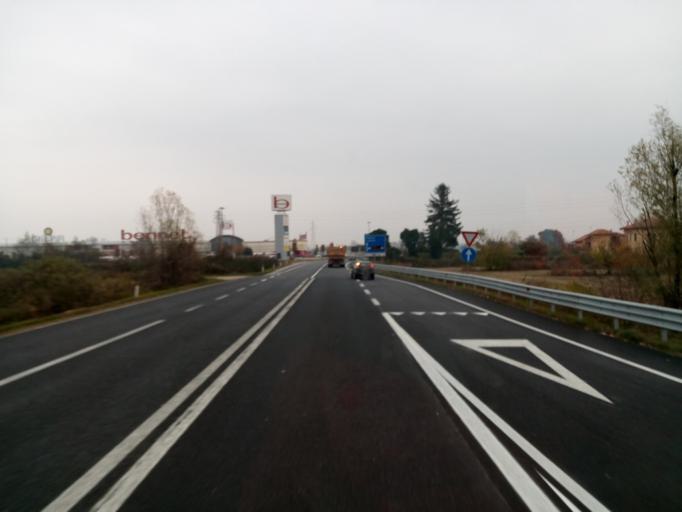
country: IT
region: Friuli Venezia Giulia
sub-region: Provincia di Udine
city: Pradamano
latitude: 46.0205
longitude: 13.2706
